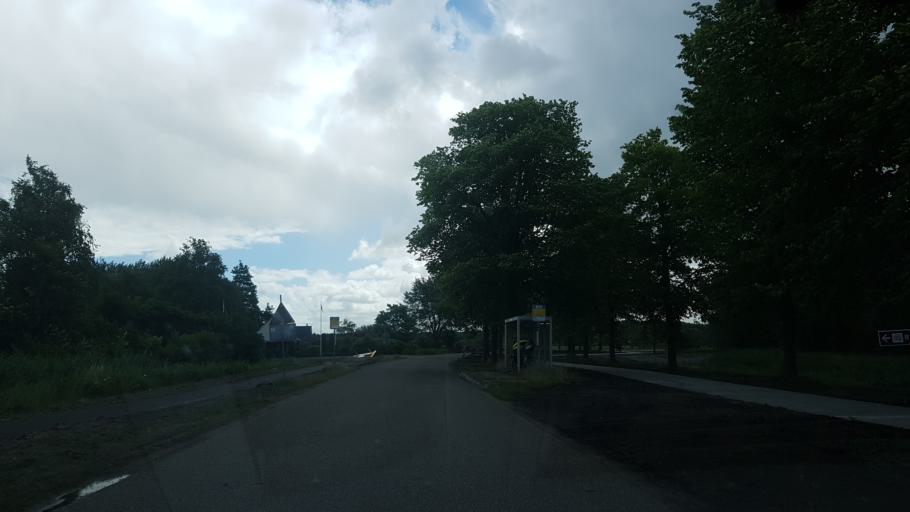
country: NL
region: Friesland
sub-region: Gemeente Dongeradeel
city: Anjum
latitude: 53.4026
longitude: 6.2174
